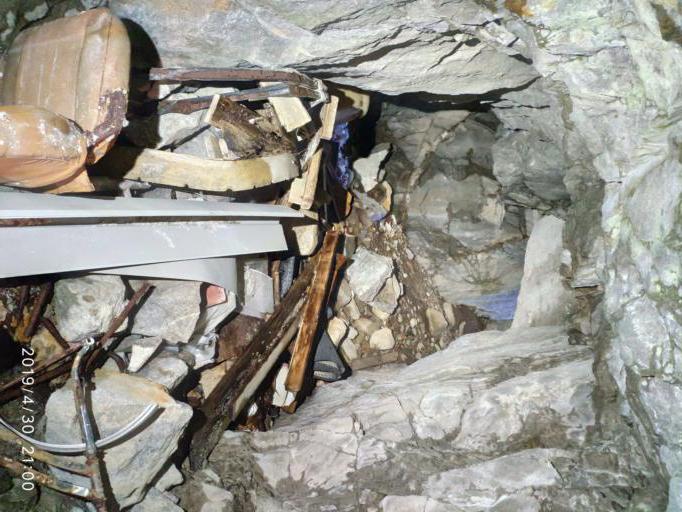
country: NO
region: Rogaland
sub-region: Eigersund
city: Egersund
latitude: 58.4745
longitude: 6.0021
